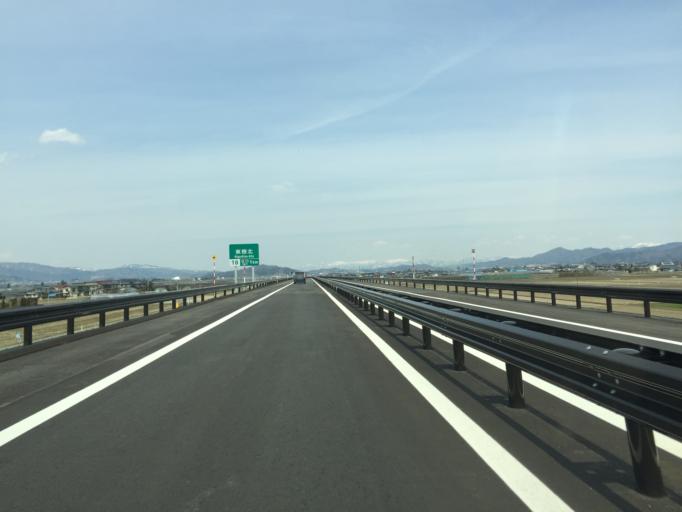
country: JP
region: Yamagata
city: Higashine
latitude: 38.4338
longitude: 140.3534
